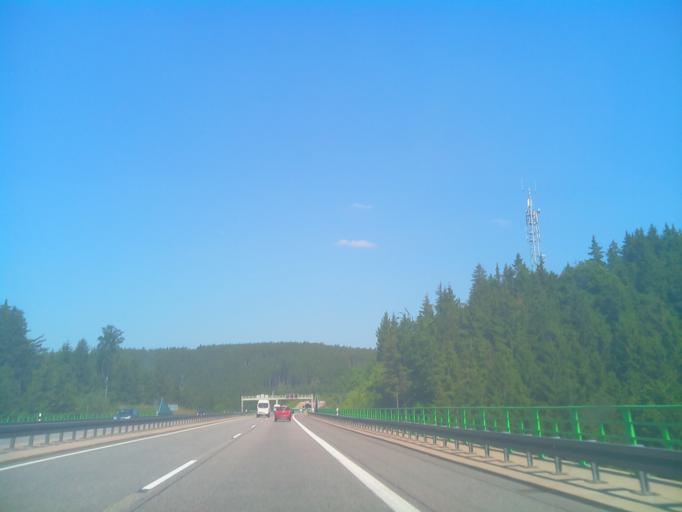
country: DE
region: Thuringia
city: Gehlberg
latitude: 50.7149
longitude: 10.7886
